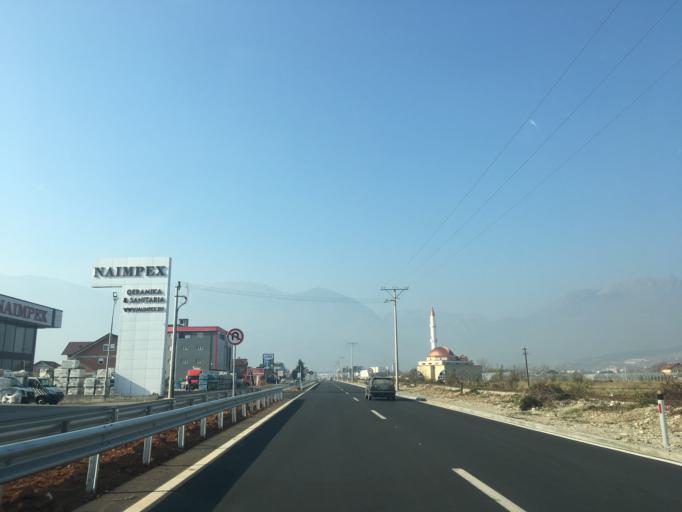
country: XK
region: Pec
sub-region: Komuna e Pejes
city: Peje
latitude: 42.6581
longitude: 20.3395
